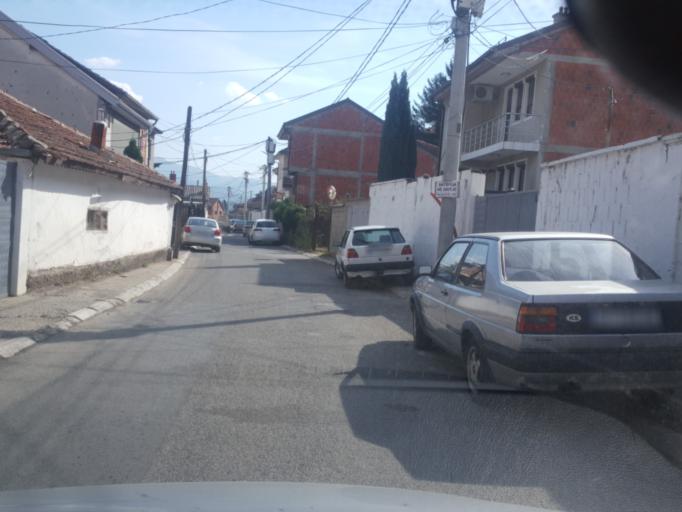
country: XK
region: Gjakova
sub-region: Komuna e Gjakoves
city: Gjakove
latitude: 42.3808
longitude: 20.4243
